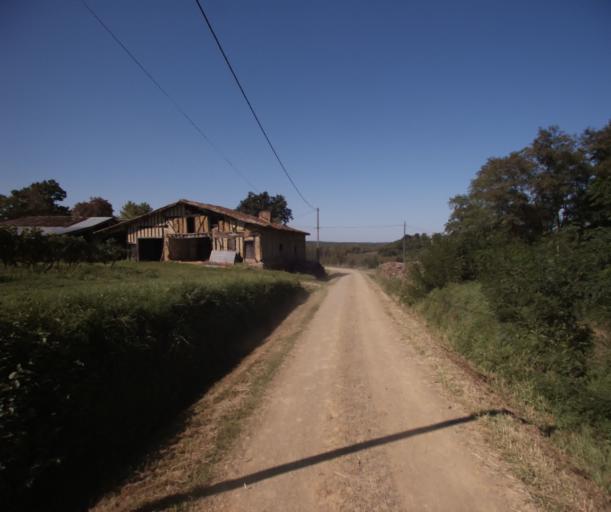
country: FR
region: Midi-Pyrenees
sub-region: Departement du Gers
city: Cazaubon
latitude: 43.9148
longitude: -0.0338
